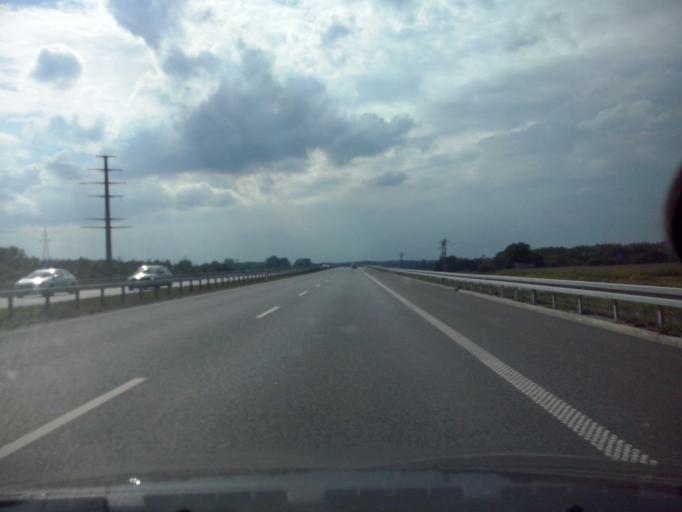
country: PL
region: Lesser Poland Voivodeship
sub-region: Powiat brzeski
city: Debno
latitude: 50.0058
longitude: 20.7250
